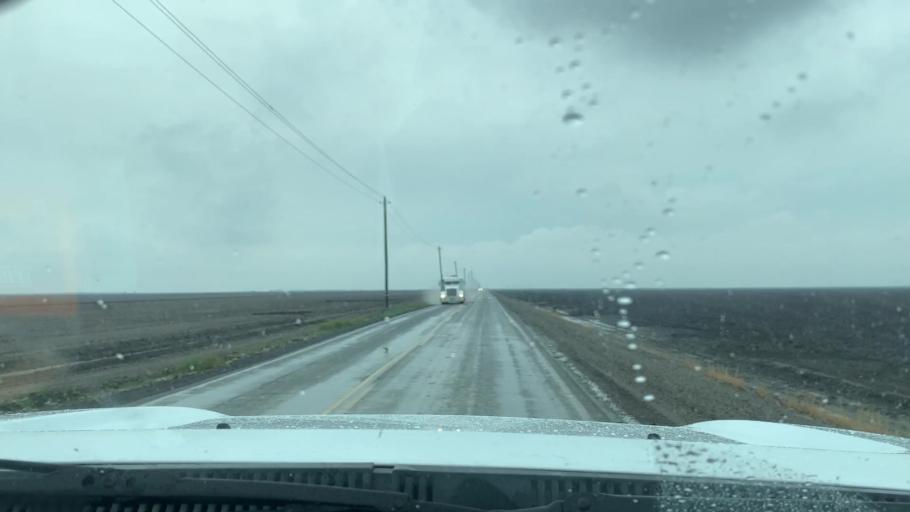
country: US
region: California
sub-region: Kings County
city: Corcoran
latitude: 35.9776
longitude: -119.5720
